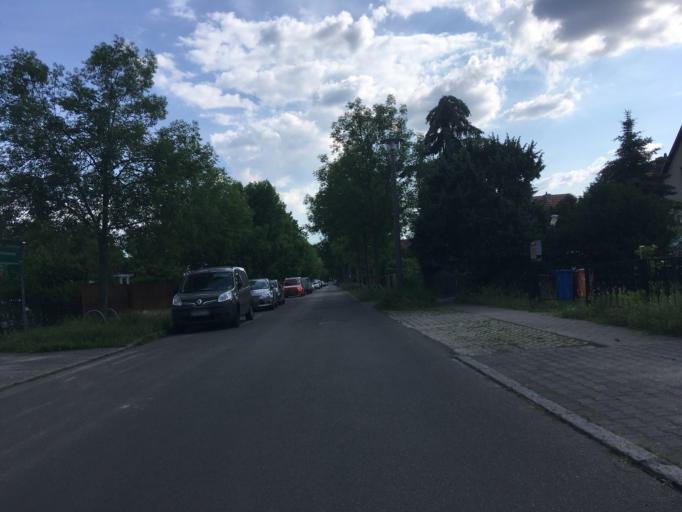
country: DE
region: Berlin
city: Adlershof
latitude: 52.4456
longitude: 13.5531
